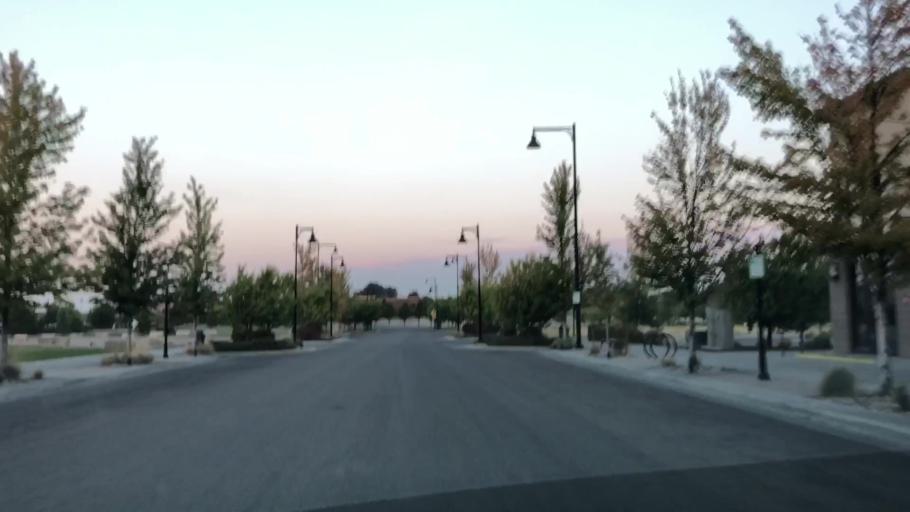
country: US
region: Idaho
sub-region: Bonneville County
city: Idaho Falls
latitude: 43.4842
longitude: -112.0529
